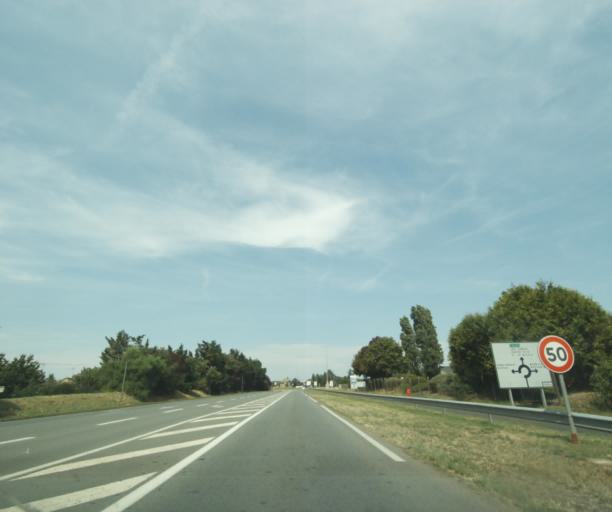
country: FR
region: Poitou-Charentes
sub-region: Departement de la Vienne
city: Dange-Saint-Romain
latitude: 46.9262
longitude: 0.6012
